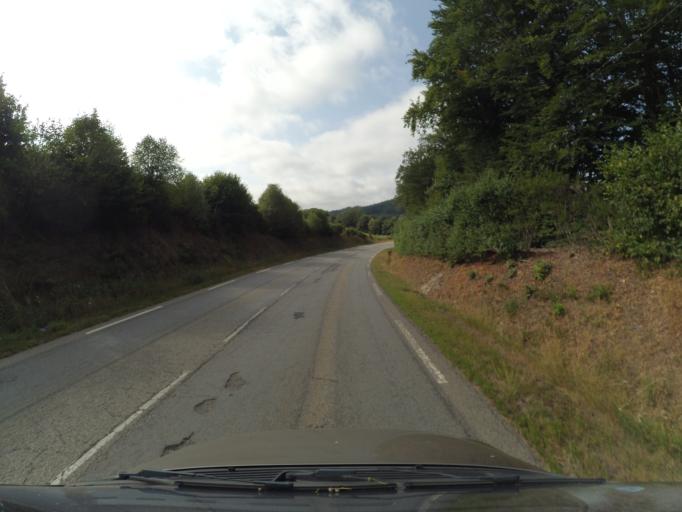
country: FR
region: Limousin
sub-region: Departement de la Correze
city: Meymac
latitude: 45.5872
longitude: 2.1305
